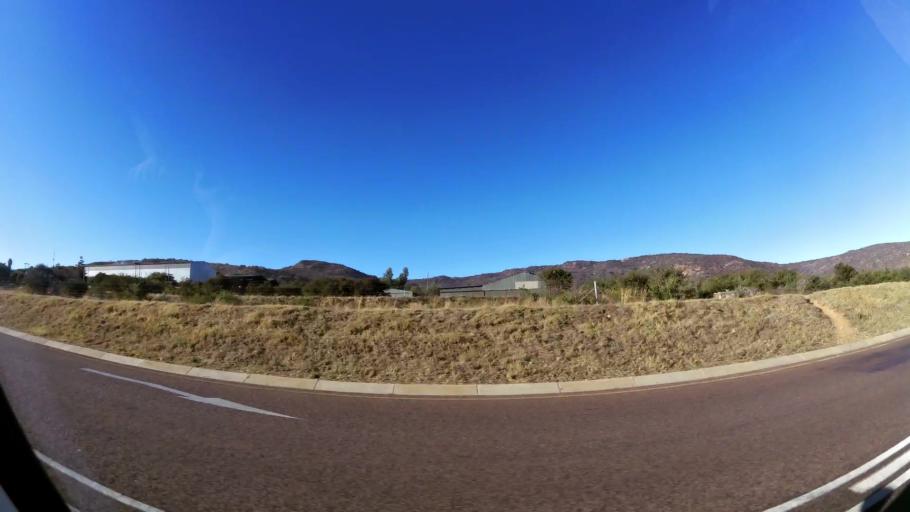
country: ZA
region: Limpopo
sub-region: Capricorn District Municipality
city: Mankoeng
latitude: -23.9296
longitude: 29.8570
